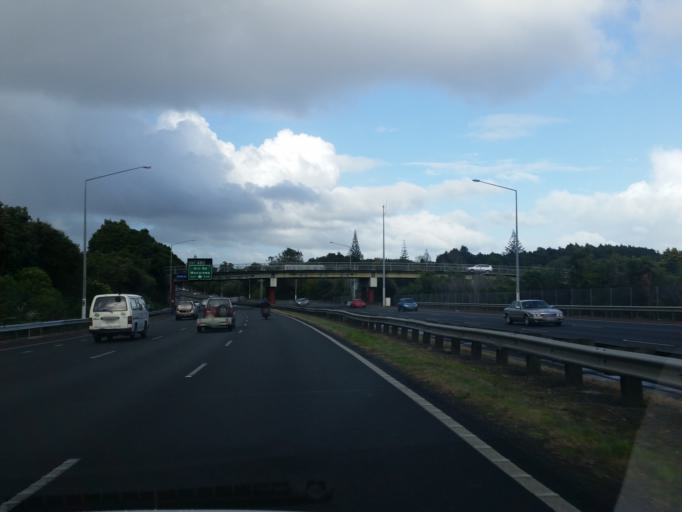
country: NZ
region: Auckland
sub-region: Auckland
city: Manukau City
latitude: -37.0054
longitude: 174.8970
